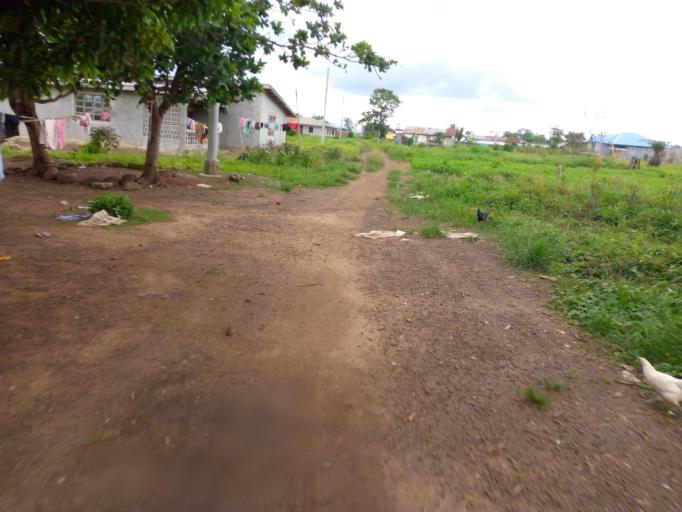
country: SL
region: Southern Province
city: Moyamba
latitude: 8.1531
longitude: -12.4402
